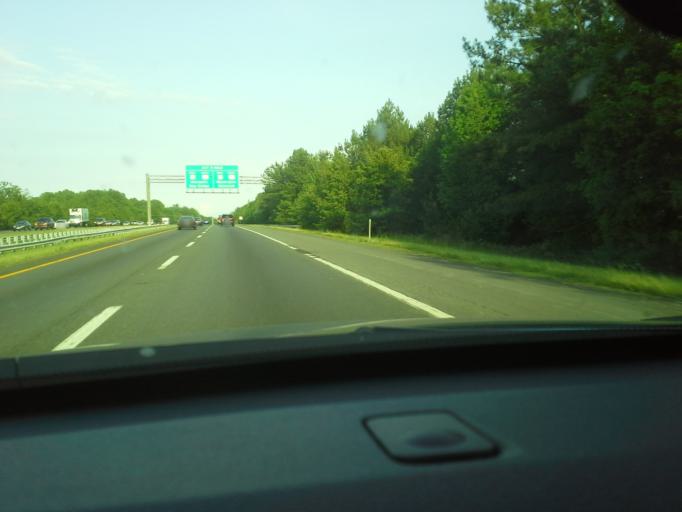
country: US
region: Maryland
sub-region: Anne Arundel County
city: Crownsville
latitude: 38.9980
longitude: -76.5915
